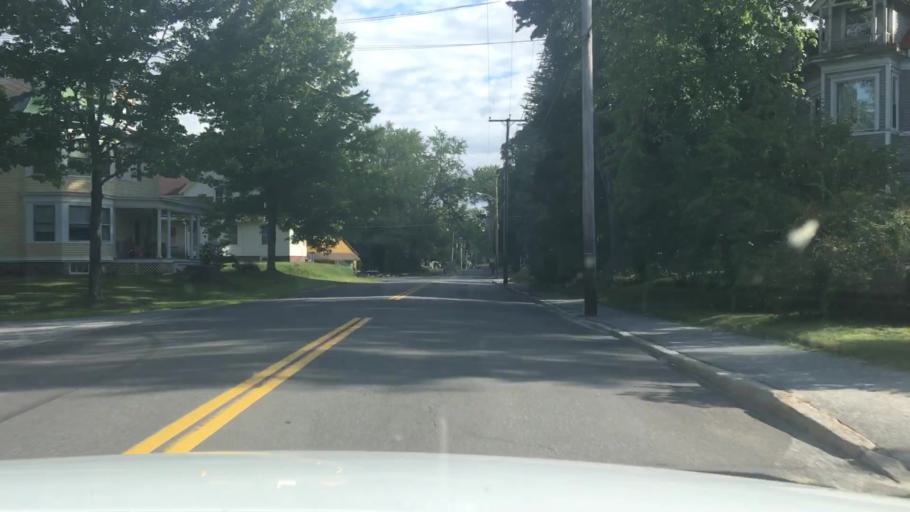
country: US
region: Maine
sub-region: Androscoggin County
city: Lisbon Falls
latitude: 44.0013
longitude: -70.0575
